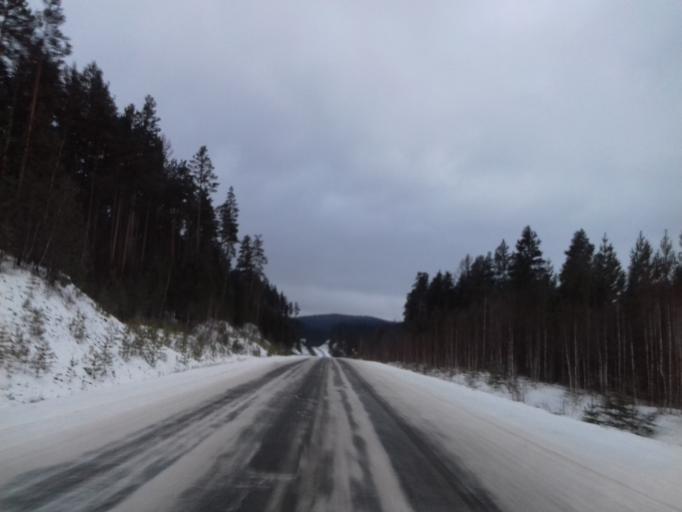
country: RU
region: Bashkortostan
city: Verkhniy Avzyan
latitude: 53.3712
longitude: 57.6466
